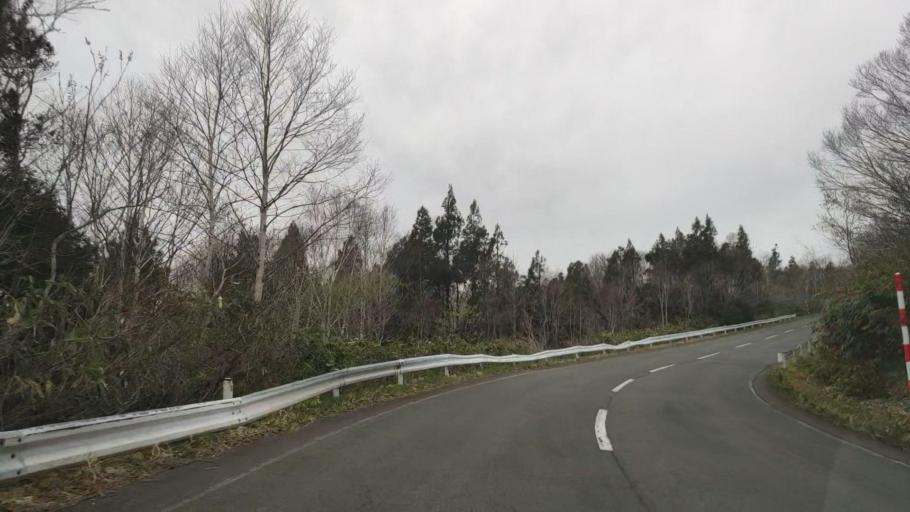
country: JP
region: Akita
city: Hanawa
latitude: 40.4154
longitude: 140.8422
